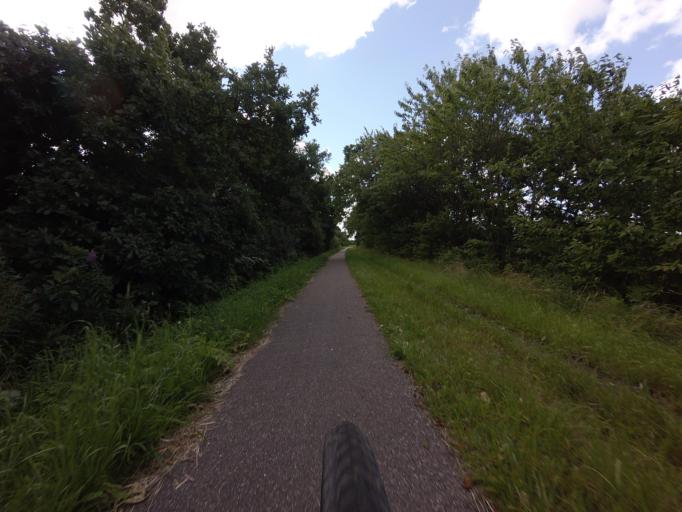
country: DK
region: Central Jutland
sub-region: Horsens Kommune
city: Horsens
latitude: 55.9104
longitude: 9.7704
